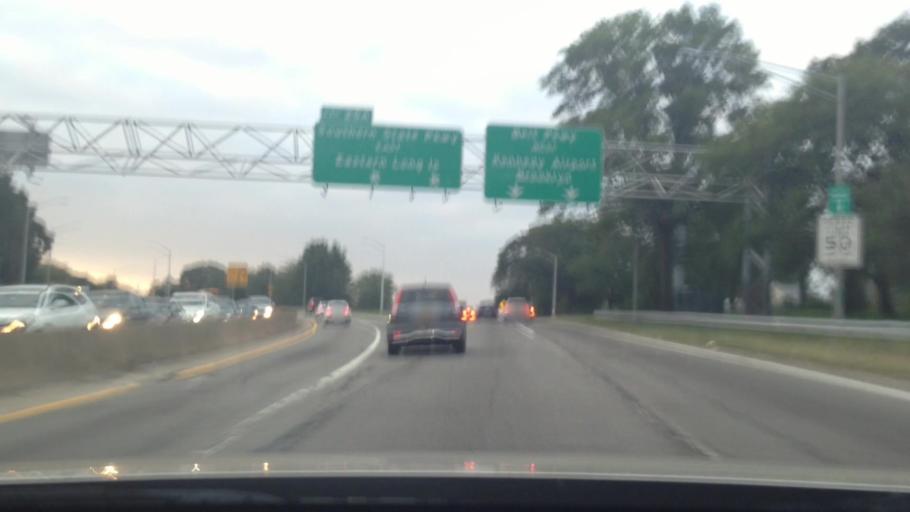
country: US
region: New York
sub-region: Nassau County
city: Elmont
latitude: 40.6899
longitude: -73.7267
